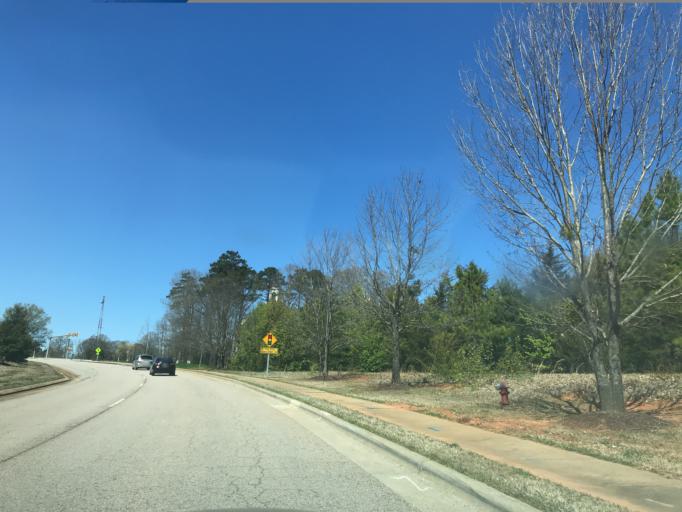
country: US
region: North Carolina
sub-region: Wake County
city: West Raleigh
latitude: 35.7752
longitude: -78.6690
